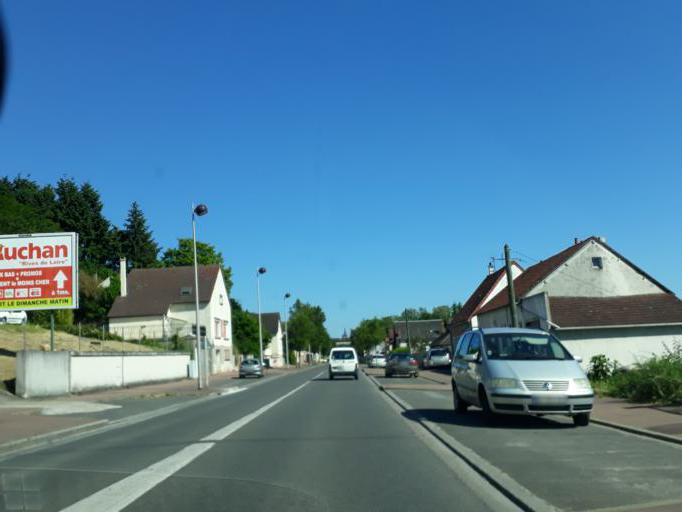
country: FR
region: Centre
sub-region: Departement du Loiret
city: Gien
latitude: 47.6946
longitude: 2.6139
